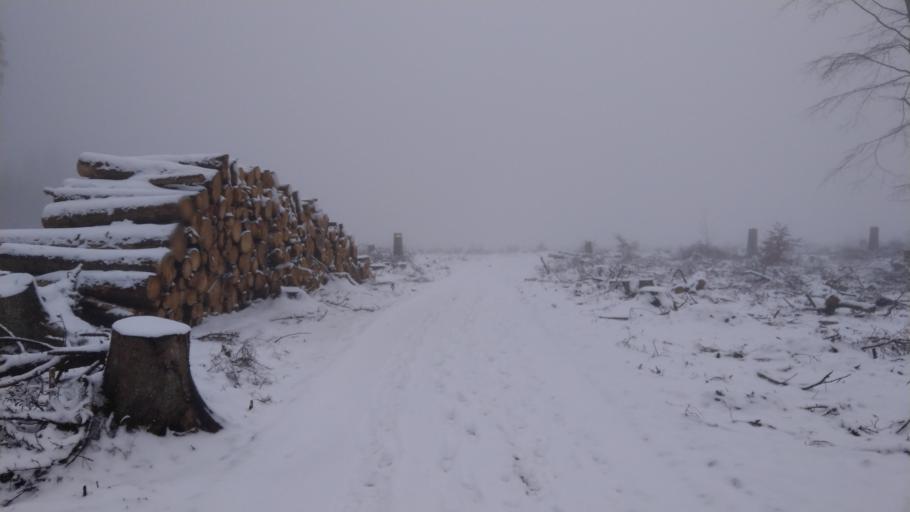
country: DE
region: North Rhine-Westphalia
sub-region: Regierungsbezirk Arnsberg
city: Erndtebruck
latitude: 50.9866
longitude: 8.2148
